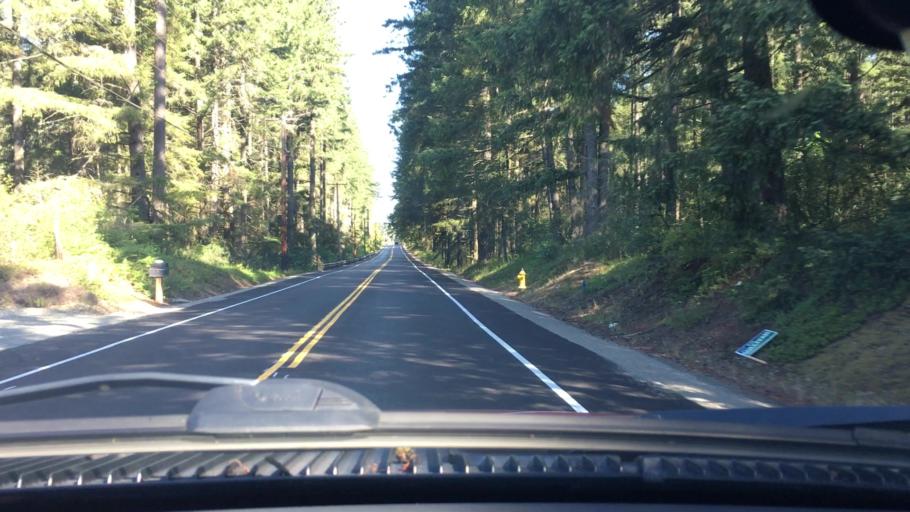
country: US
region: Washington
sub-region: King County
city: Lake Morton-Berrydale
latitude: 47.3183
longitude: -122.1029
